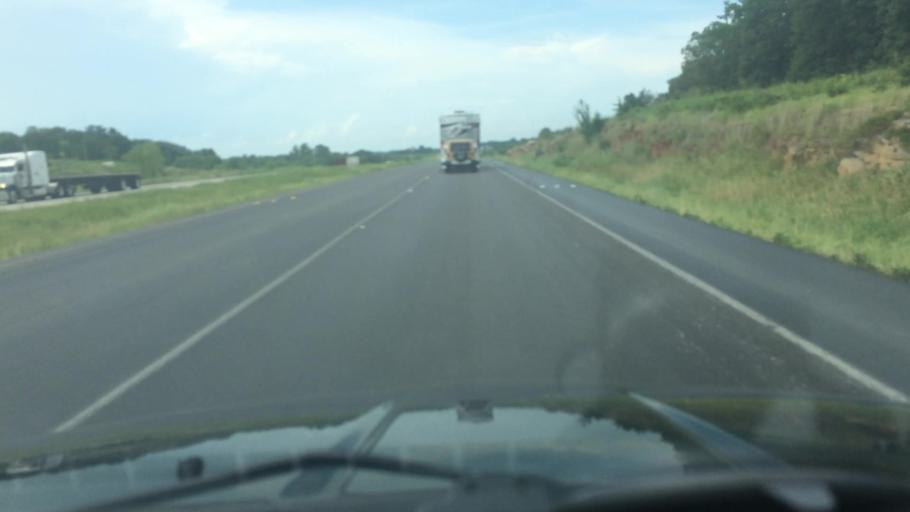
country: US
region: Missouri
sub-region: Saint Clair County
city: Osceola
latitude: 37.9804
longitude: -93.6491
